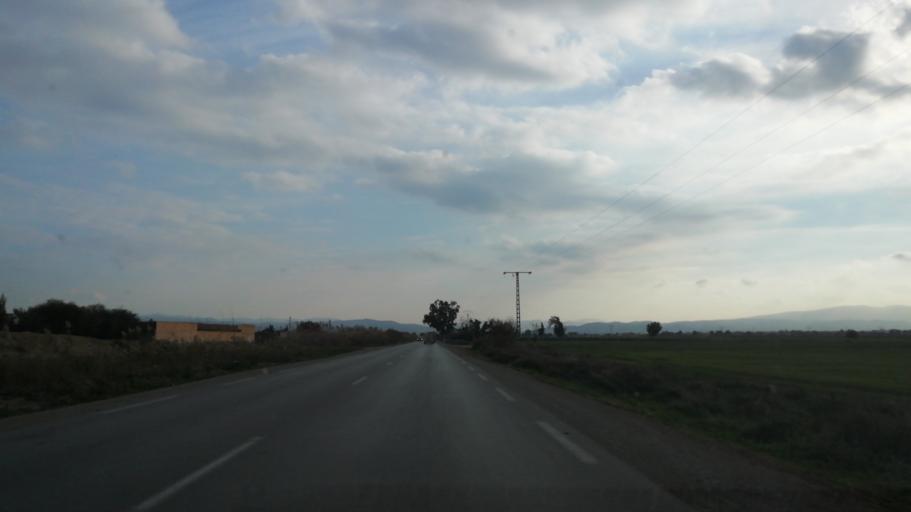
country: DZ
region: Mascara
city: Mascara
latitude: 35.6486
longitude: 0.0596
